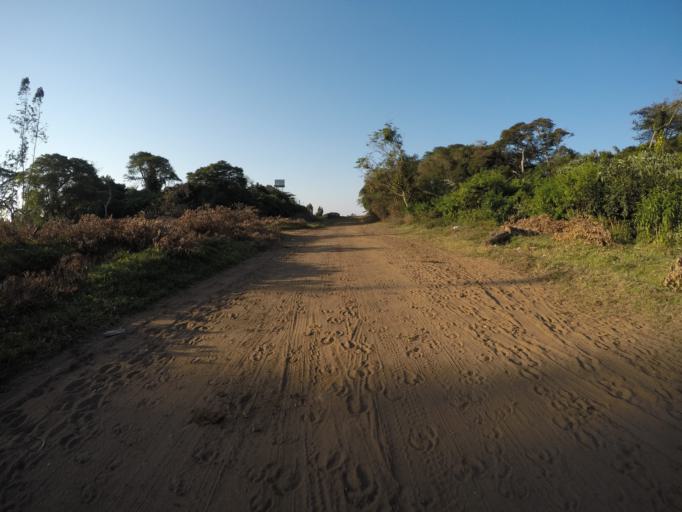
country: ZA
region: KwaZulu-Natal
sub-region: uThungulu District Municipality
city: KwaMbonambi
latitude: -28.6947
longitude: 32.1976
